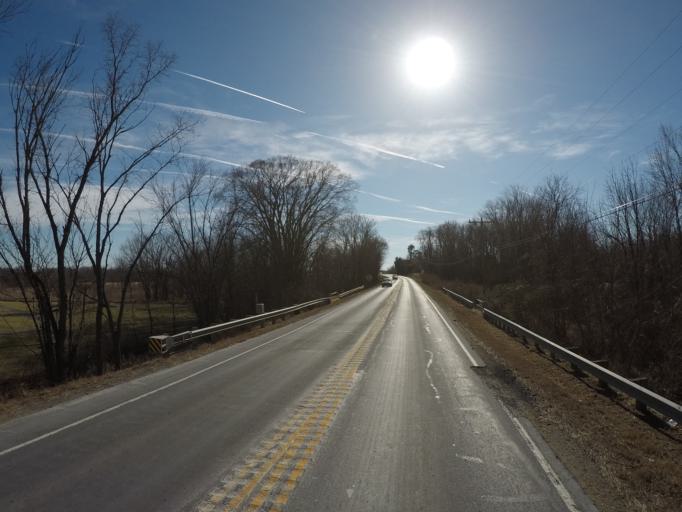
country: US
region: Maryland
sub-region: Frederick County
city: Point of Rocks
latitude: 39.2121
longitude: -77.5356
